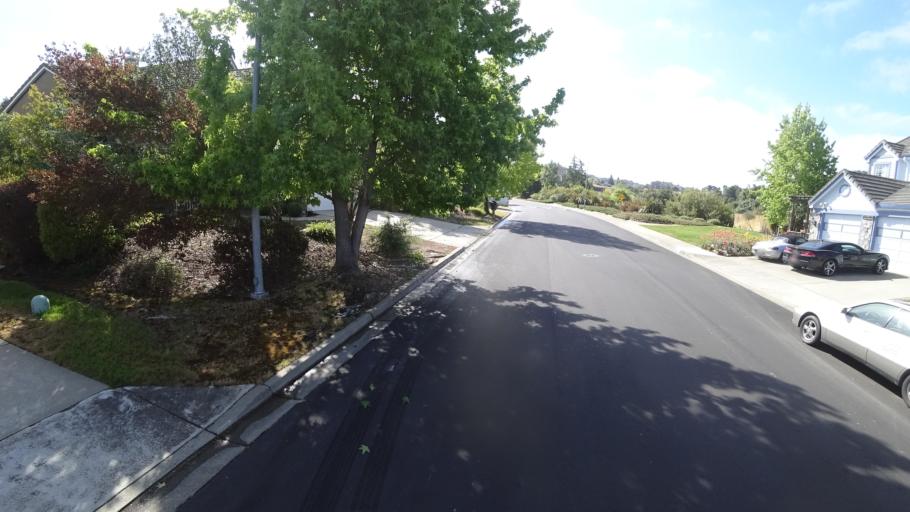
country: US
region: California
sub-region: Alameda County
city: Fairview
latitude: 37.6594
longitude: -122.0207
